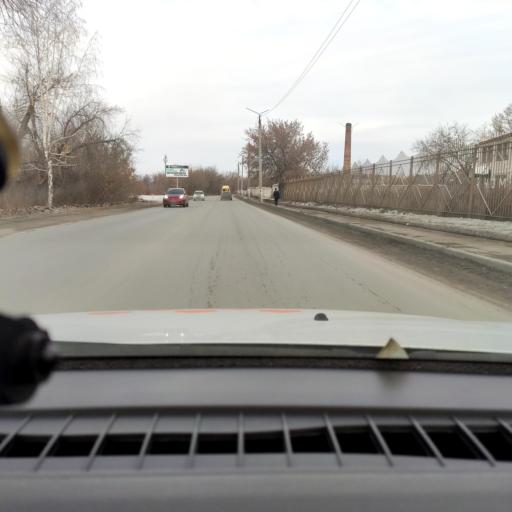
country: RU
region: Samara
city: Chapayevsk
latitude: 52.9662
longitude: 49.6938
